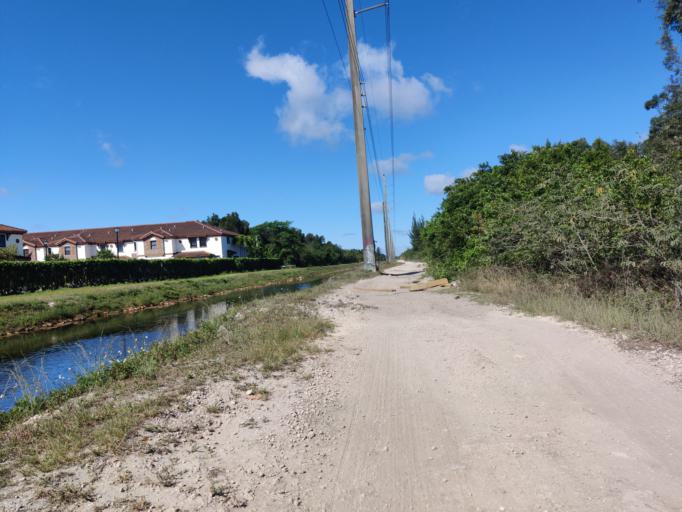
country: US
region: Florida
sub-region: Miami-Dade County
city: Kendall West
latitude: 25.7275
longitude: -80.4625
